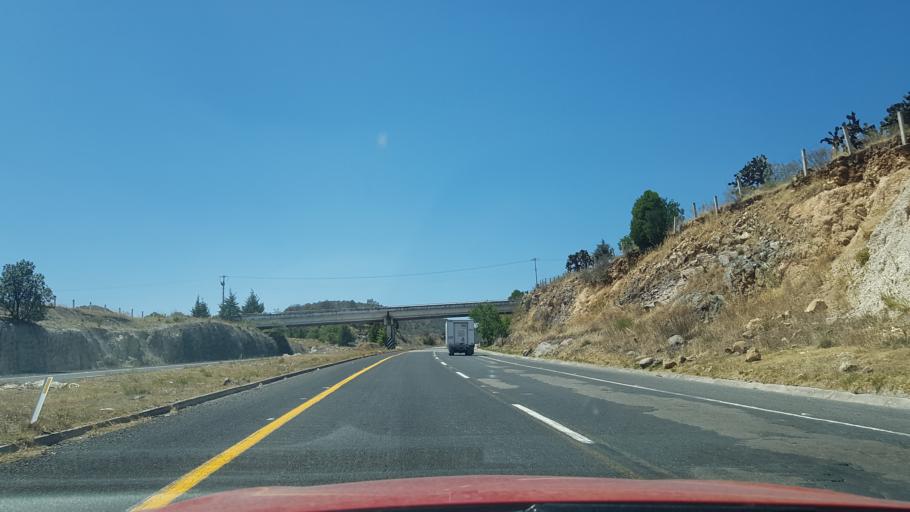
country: MX
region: Mexico
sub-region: Atlacomulco
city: La Mesa de Chosto
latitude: 19.8579
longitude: -99.8785
